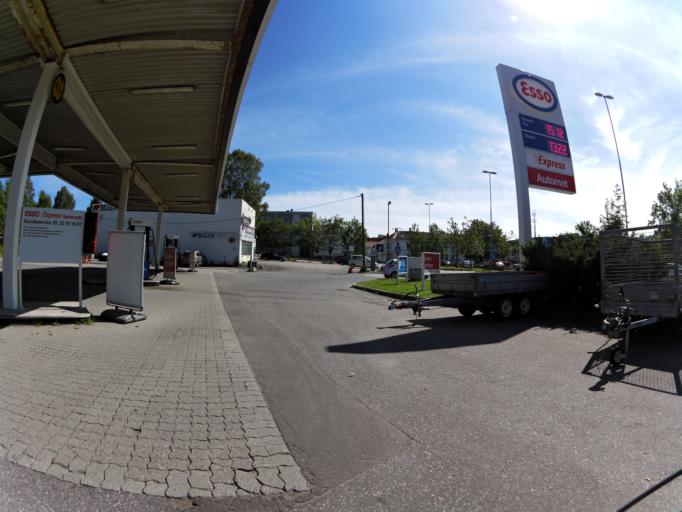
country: NO
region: Ostfold
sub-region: Fredrikstad
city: Fredrikstad
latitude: 59.2155
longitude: 10.9420
